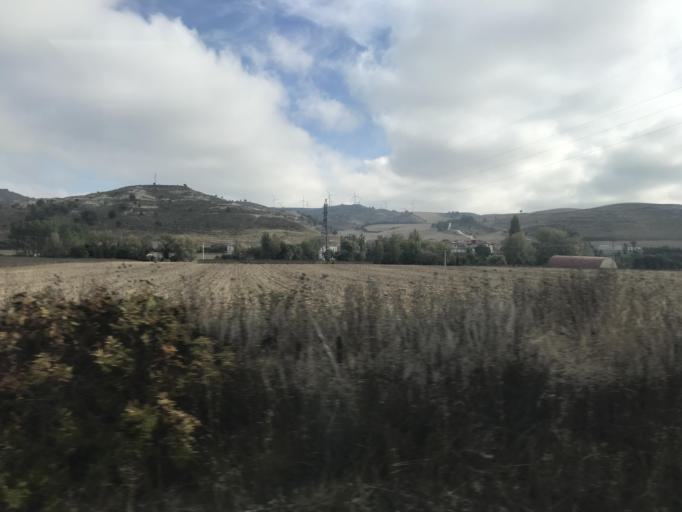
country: ES
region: Castille and Leon
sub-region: Provincia de Burgos
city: Santa Maria del Invierno
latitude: 42.4410
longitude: -3.4443
